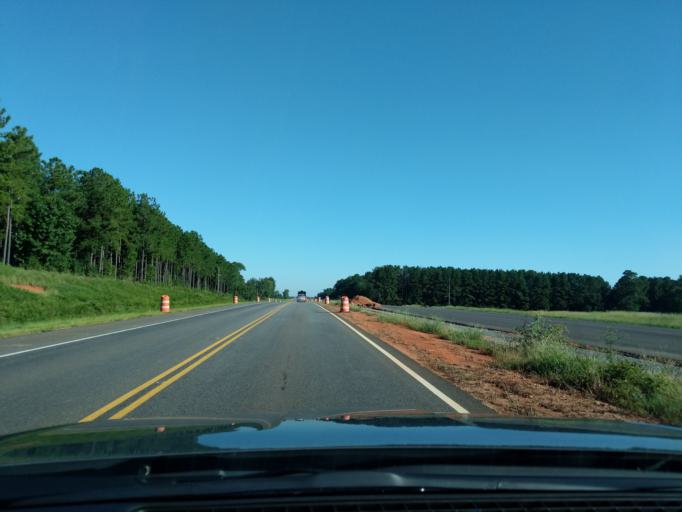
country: US
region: Georgia
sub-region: McDuffie County
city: Thomson
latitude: 33.5560
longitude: -82.5131
